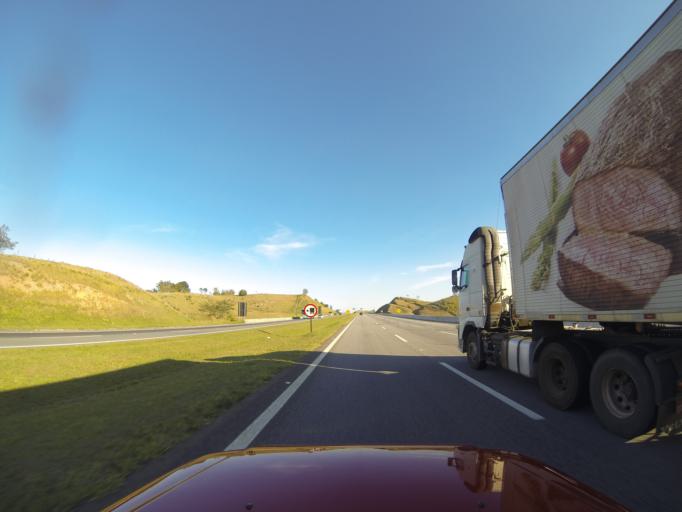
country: BR
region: Sao Paulo
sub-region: Jacarei
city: Jacarei
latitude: -23.2961
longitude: -46.0471
